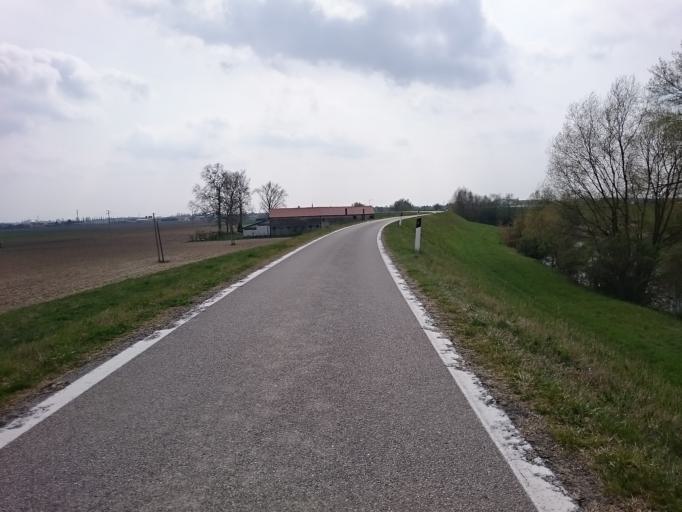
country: IT
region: Veneto
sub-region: Provincia di Padova
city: Bovolenta
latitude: 45.2858
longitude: 11.9319
